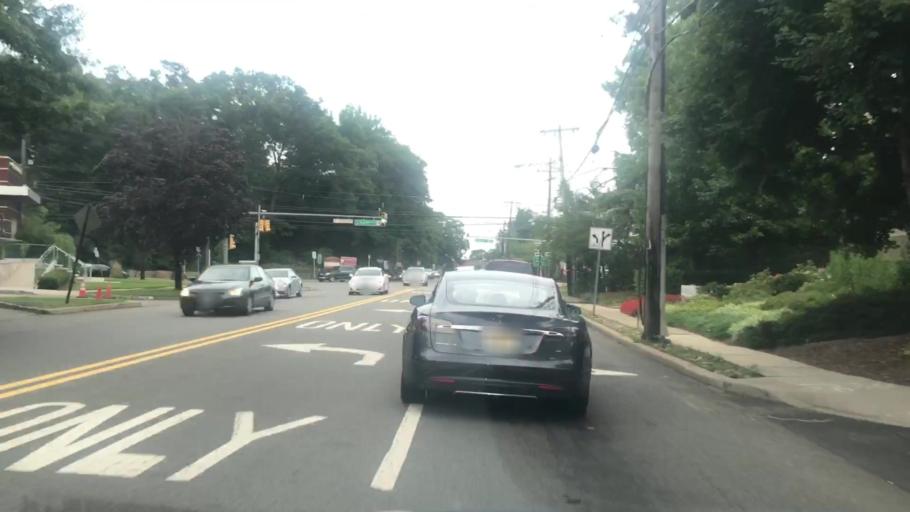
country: US
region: New Jersey
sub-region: Bergen County
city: Englewood Cliffs
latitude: 40.8810
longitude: -73.9521
